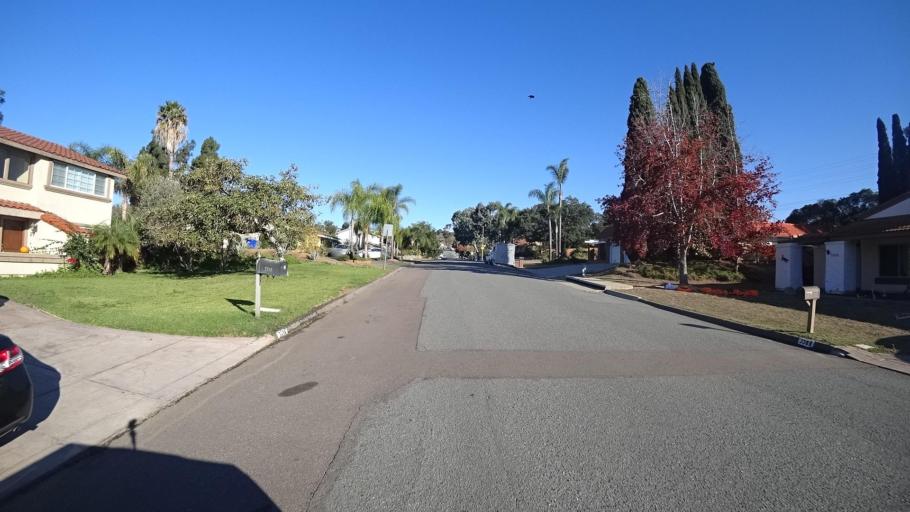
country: US
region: California
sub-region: San Diego County
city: Bonita
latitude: 32.6723
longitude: -117.0298
